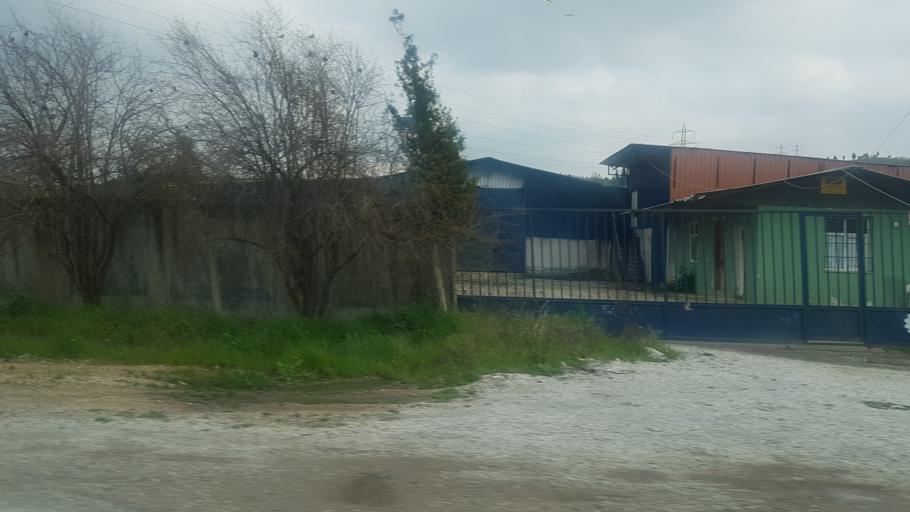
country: TR
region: Mersin
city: Yenice
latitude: 37.0652
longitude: 35.1710
